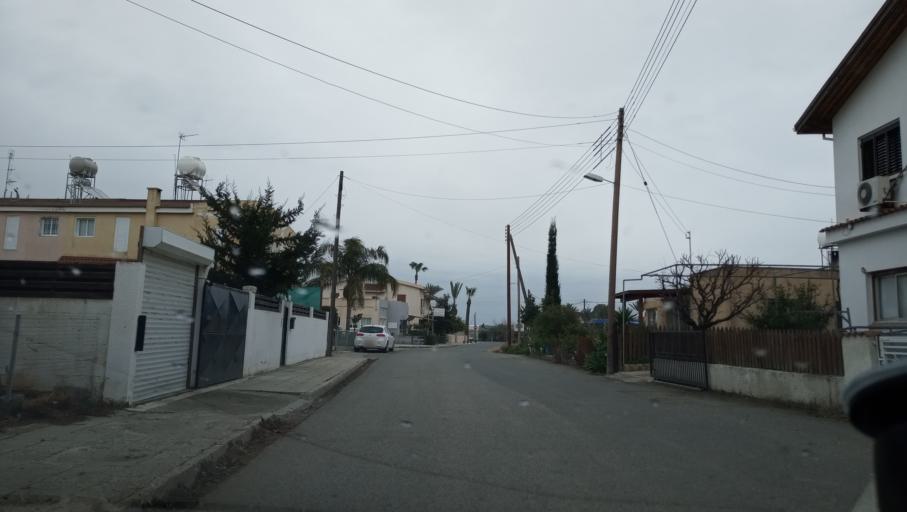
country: CY
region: Lefkosia
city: Kato Deftera
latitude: 35.0817
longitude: 33.2722
